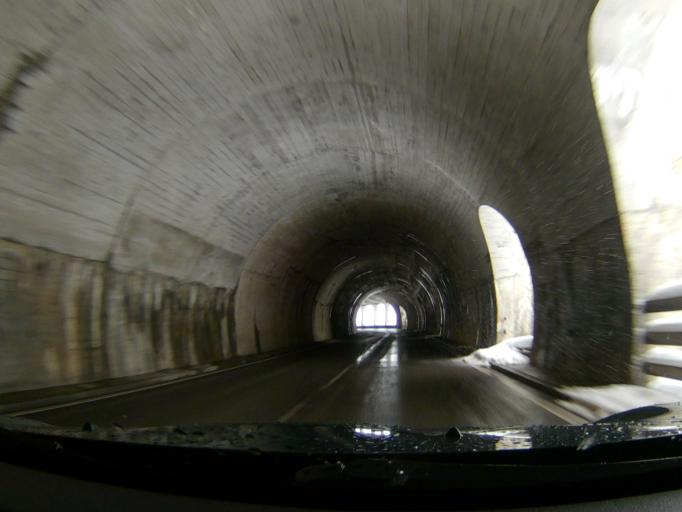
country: AT
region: Vorarlberg
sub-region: Politischer Bezirk Bregenz
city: Schroecken
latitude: 47.2671
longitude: 10.0663
